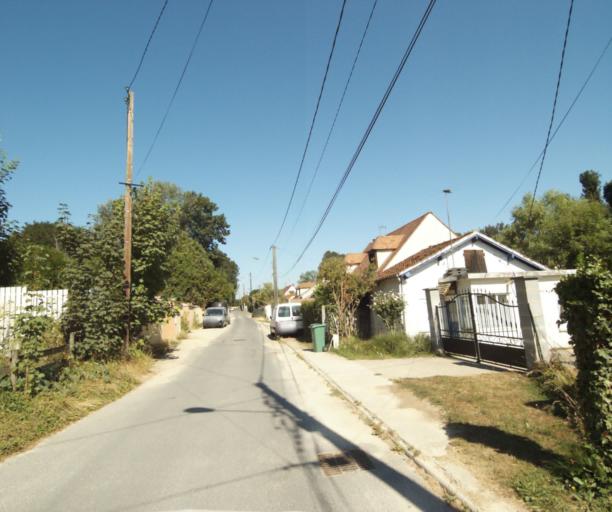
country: FR
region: Ile-de-France
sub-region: Departement de l'Essonne
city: Itteville
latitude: 48.5317
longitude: 2.3573
